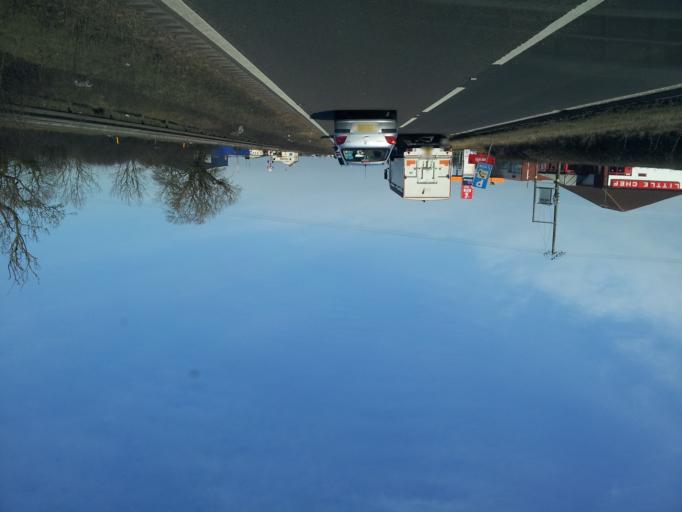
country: GB
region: England
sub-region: District of Rutland
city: Greetham
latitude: 52.7630
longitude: -0.6108
